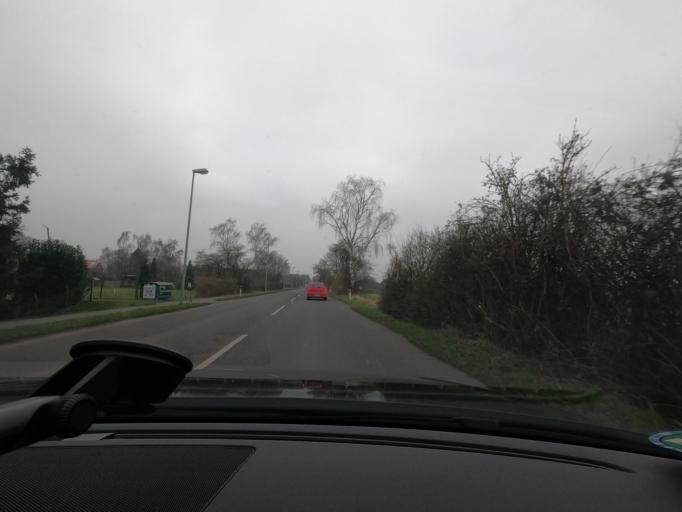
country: DE
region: North Rhine-Westphalia
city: Tonisvorst
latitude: 51.3927
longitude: 6.4985
